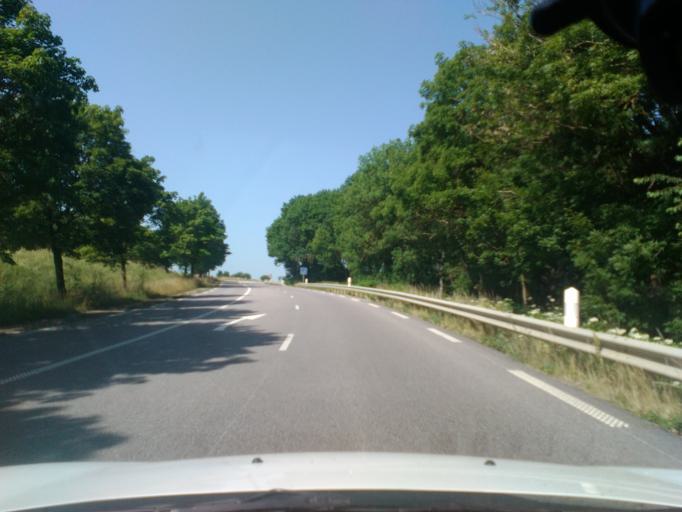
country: FR
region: Lorraine
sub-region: Departement des Vosges
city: Chatenois
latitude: 48.3029
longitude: 5.8189
